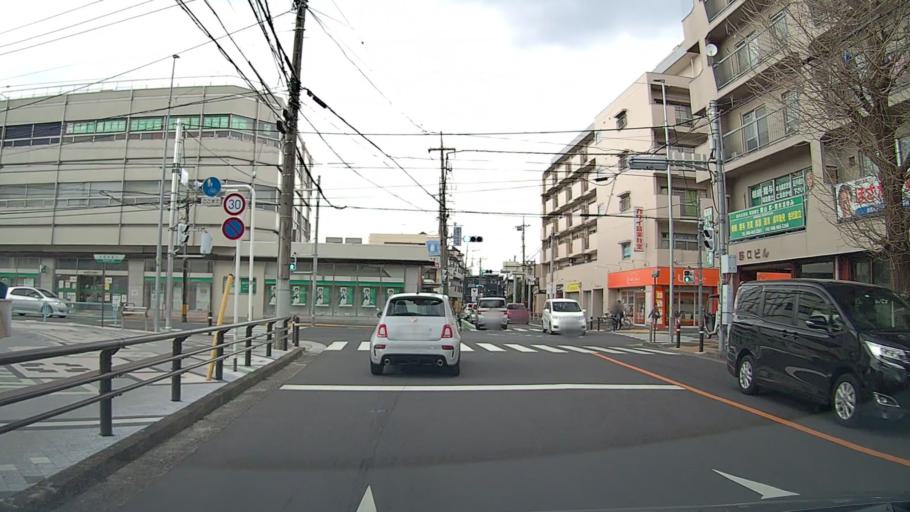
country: JP
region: Saitama
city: Asaka
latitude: 35.7972
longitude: 139.5947
